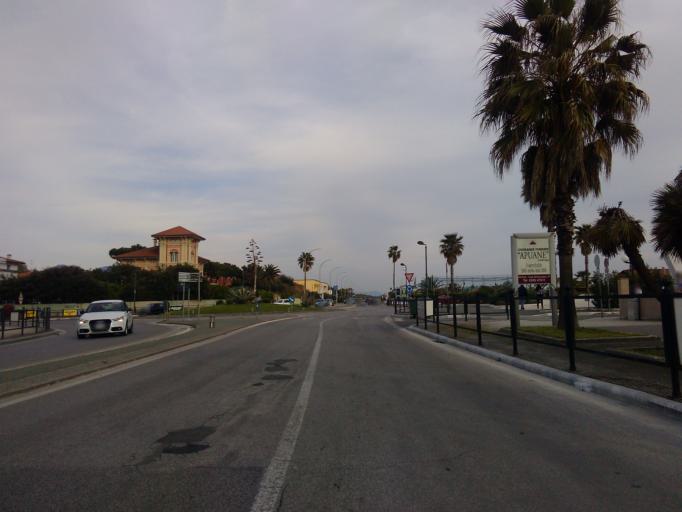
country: IT
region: Tuscany
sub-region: Provincia di Massa-Carrara
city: Massa
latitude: 44.0029
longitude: 10.1070
